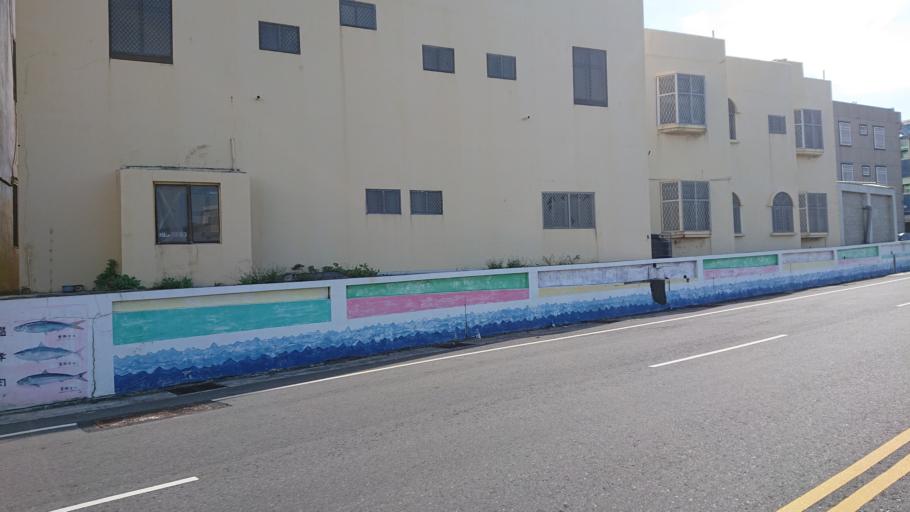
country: TW
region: Taiwan
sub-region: Penghu
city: Ma-kung
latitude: 23.5266
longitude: 119.5701
